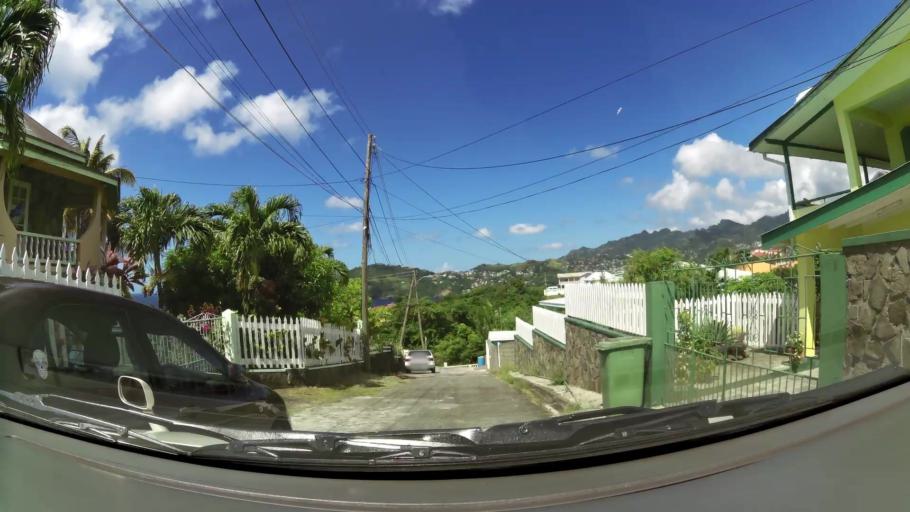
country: VC
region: Saint George
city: Kingstown
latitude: 13.1411
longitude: -61.2261
